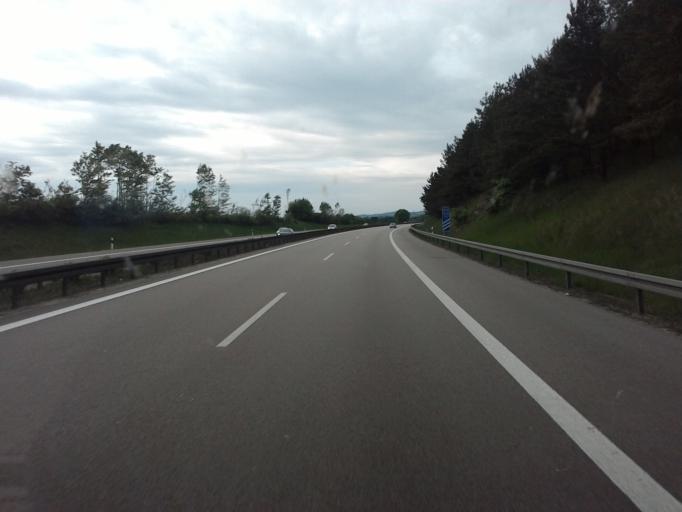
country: DE
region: Bavaria
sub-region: Upper Palatinate
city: Velburg
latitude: 49.2283
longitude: 11.6406
